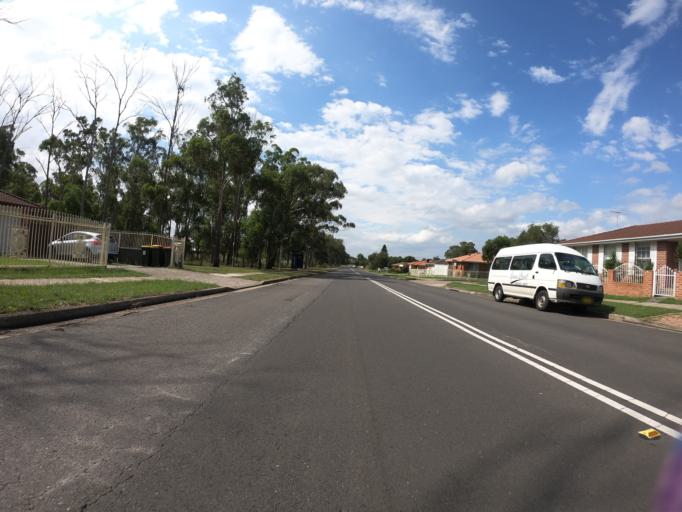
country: AU
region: New South Wales
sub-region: Blacktown
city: Hassall Grove
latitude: -33.7405
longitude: 150.8356
